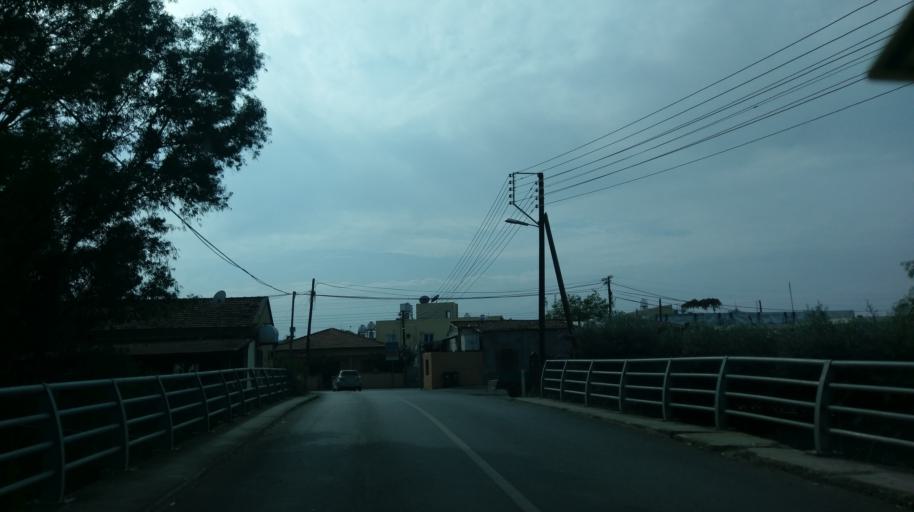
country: CY
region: Lefkosia
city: Morfou
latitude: 35.1683
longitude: 33.0094
